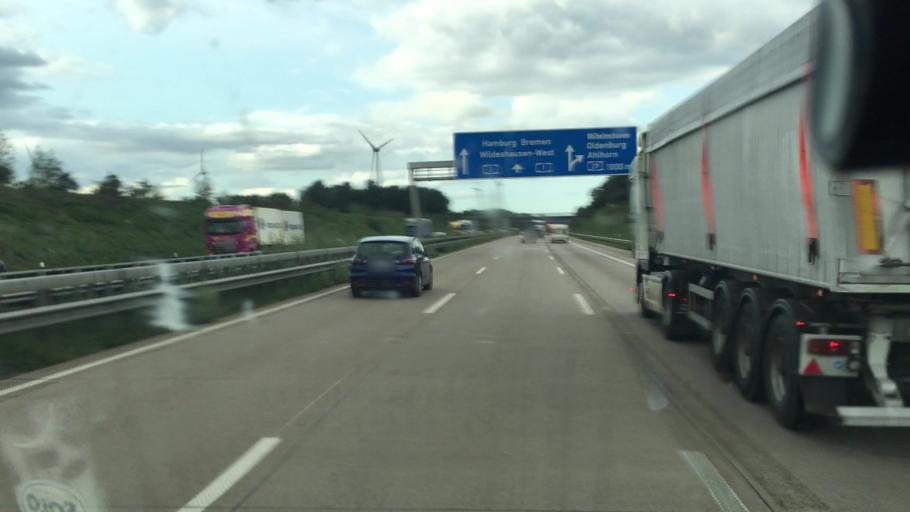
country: DE
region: Lower Saxony
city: Buehren
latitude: 52.8354
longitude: 8.2175
